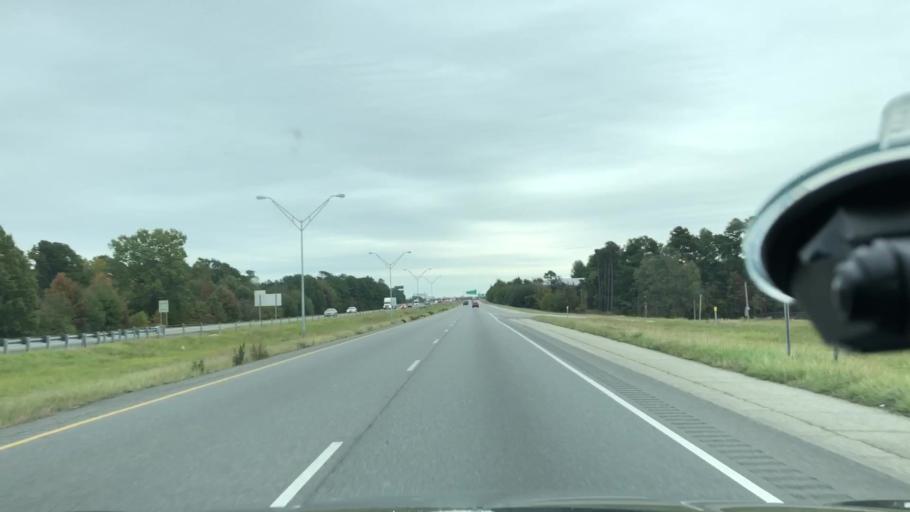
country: US
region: Arkansas
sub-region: Miller County
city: Texarkana
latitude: 33.4762
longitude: -94.0051
